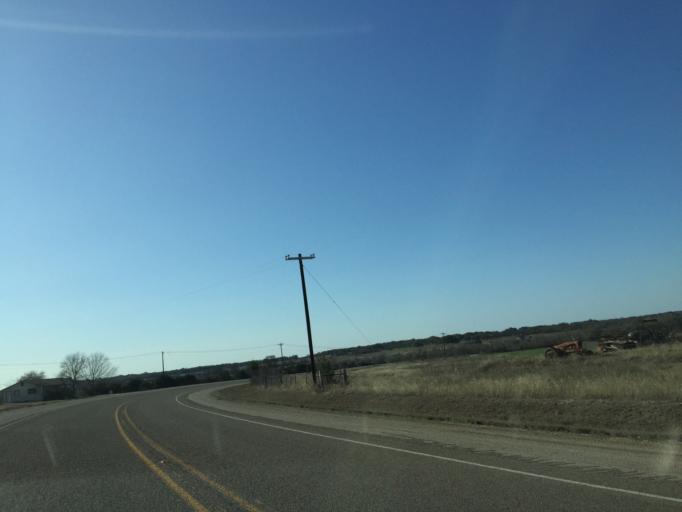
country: US
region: Texas
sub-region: Williamson County
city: Florence
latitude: 30.7649
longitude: -97.8428
